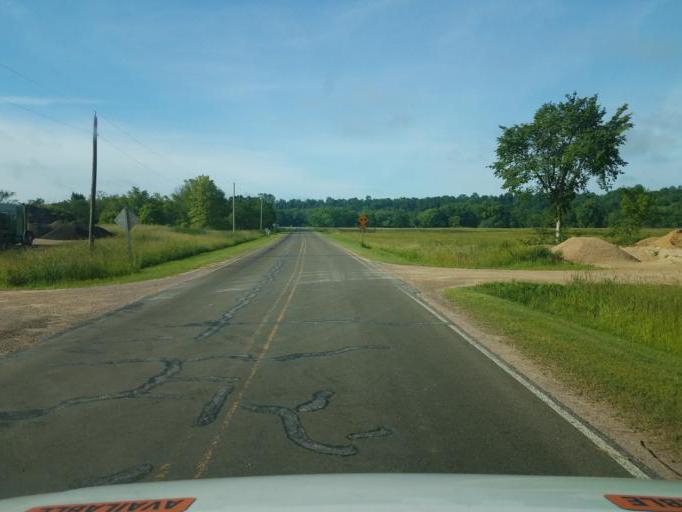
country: US
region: Wisconsin
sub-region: Juneau County
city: Elroy
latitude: 43.6457
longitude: -90.2219
